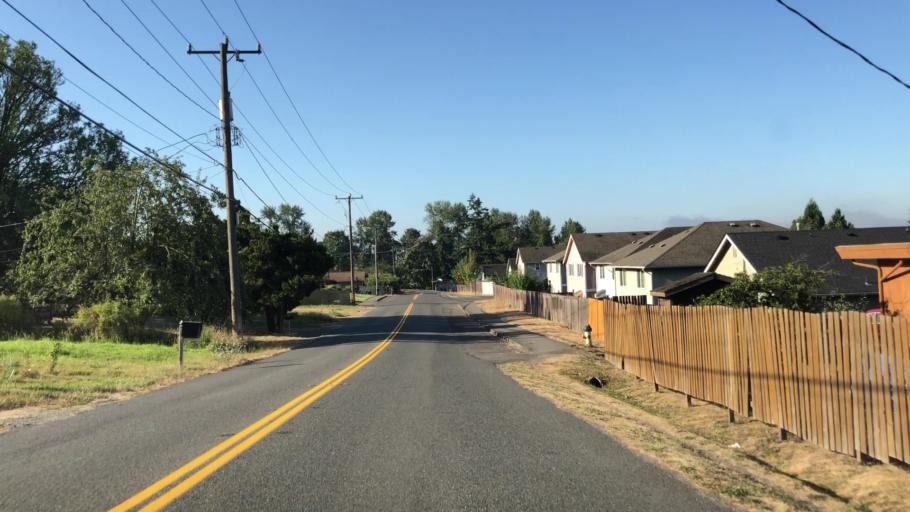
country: US
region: Washington
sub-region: King County
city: Bryn Mawr-Skyway
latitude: 47.4949
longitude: -122.2596
